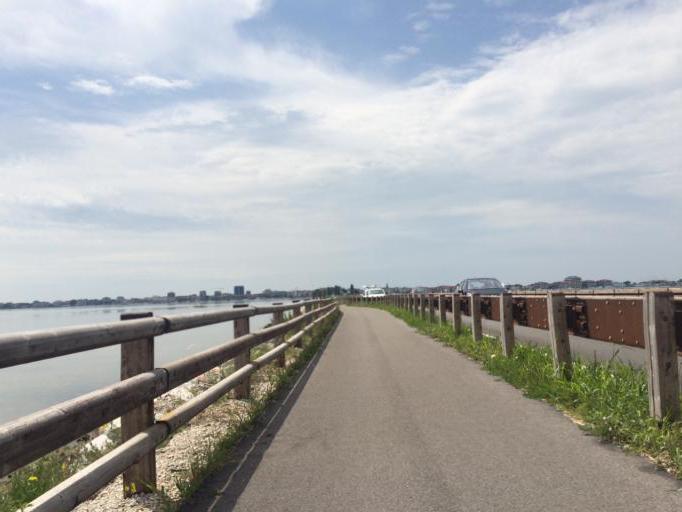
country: IT
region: Friuli Venezia Giulia
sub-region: Provincia di Gorizia
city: Grado
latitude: 45.6947
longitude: 13.3840
